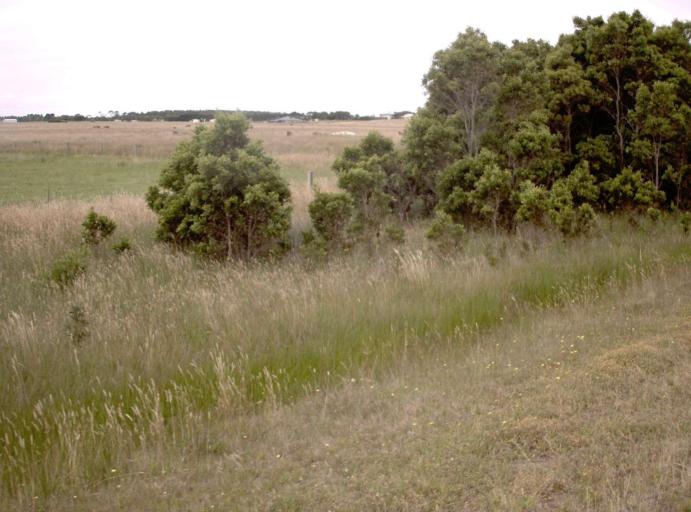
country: AU
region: Victoria
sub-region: Wellington
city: Sale
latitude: -38.5480
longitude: 146.9691
